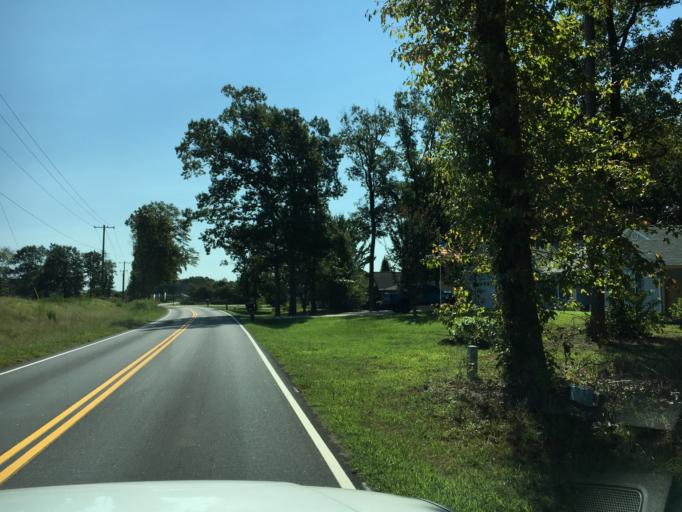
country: US
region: South Carolina
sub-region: Spartanburg County
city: Duncan
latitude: 34.8946
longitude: -82.1228
